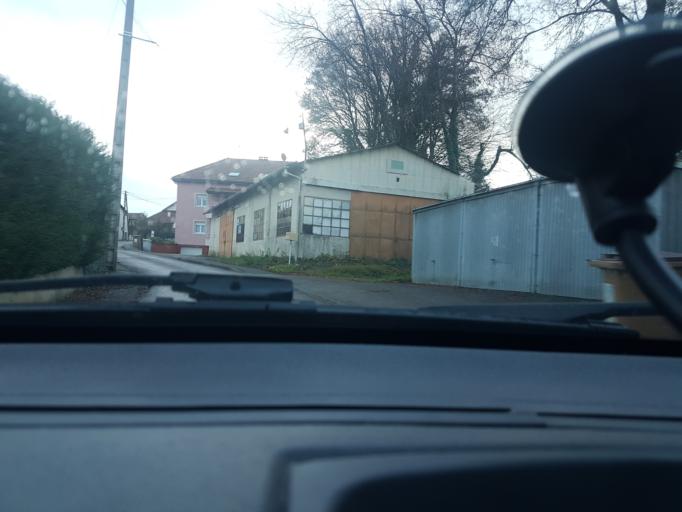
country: FR
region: Franche-Comte
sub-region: Territoire de Belfort
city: Bavilliers
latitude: 47.6227
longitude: 6.8332
